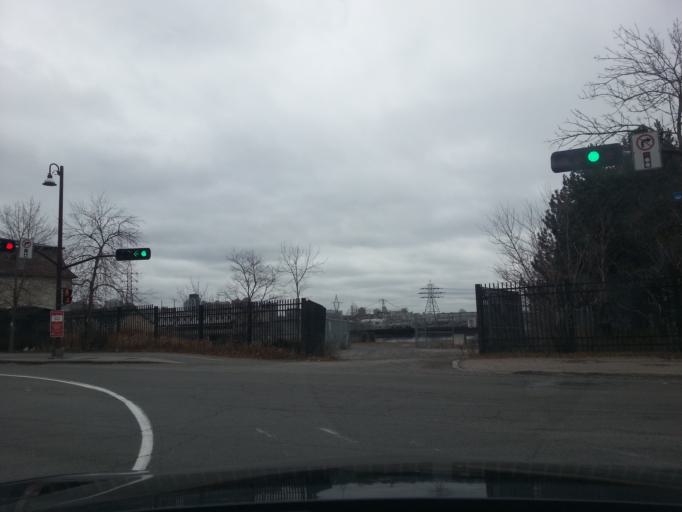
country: CA
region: Ontario
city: Ottawa
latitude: 45.4246
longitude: -75.7230
